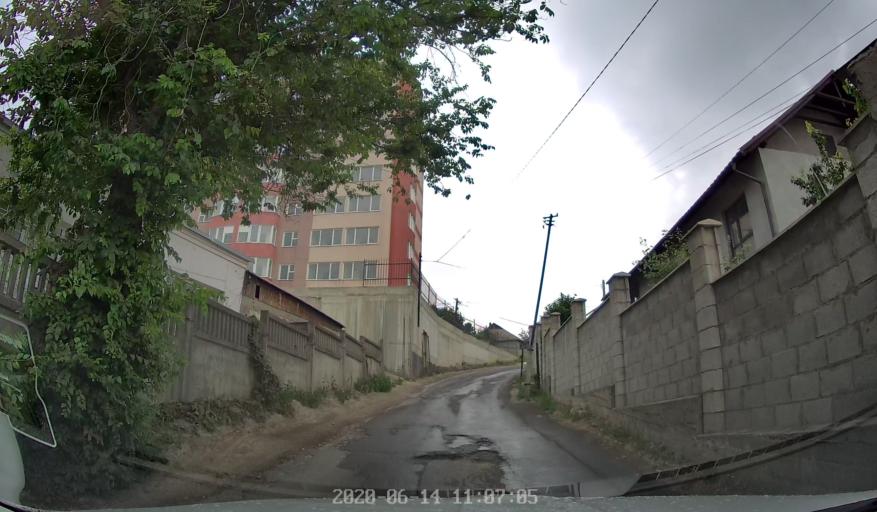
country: MD
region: Chisinau
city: Chisinau
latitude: 47.0450
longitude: 28.8356
